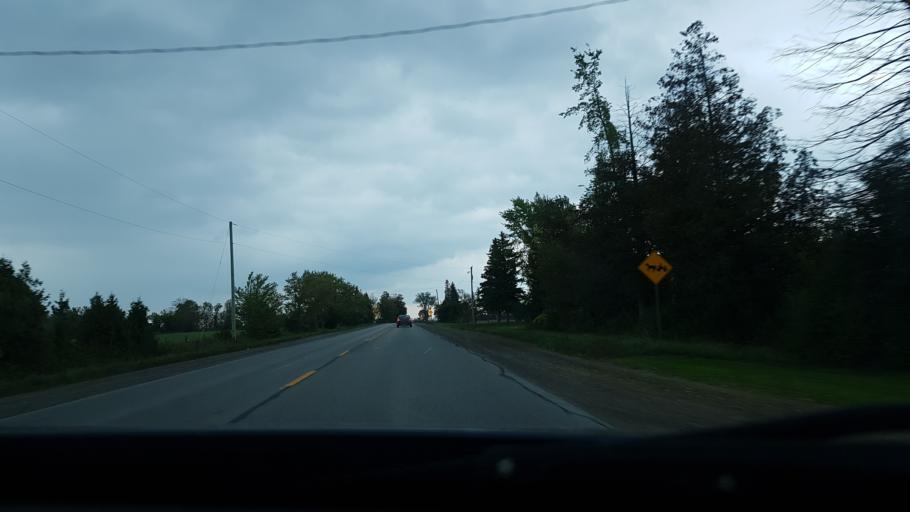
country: CA
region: Ontario
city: Omemee
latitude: 44.3758
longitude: -78.6472
